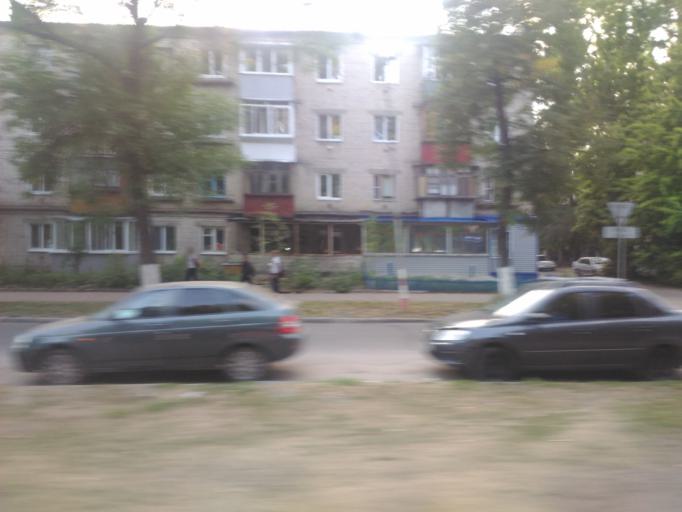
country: RU
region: Ulyanovsk
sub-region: Ulyanovskiy Rayon
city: Ulyanovsk
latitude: 54.3026
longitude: 48.3222
